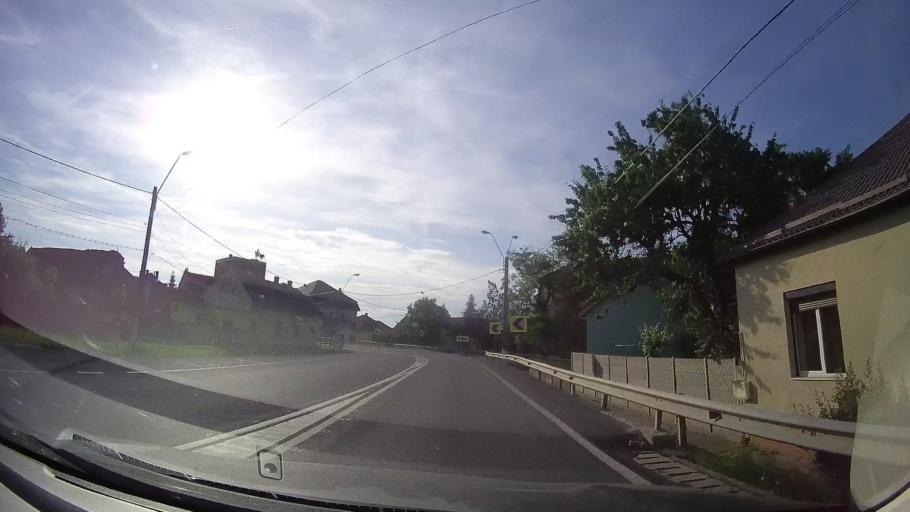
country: RO
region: Timis
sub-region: Oras Recas
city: Recas
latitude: 45.8003
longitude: 21.5130
